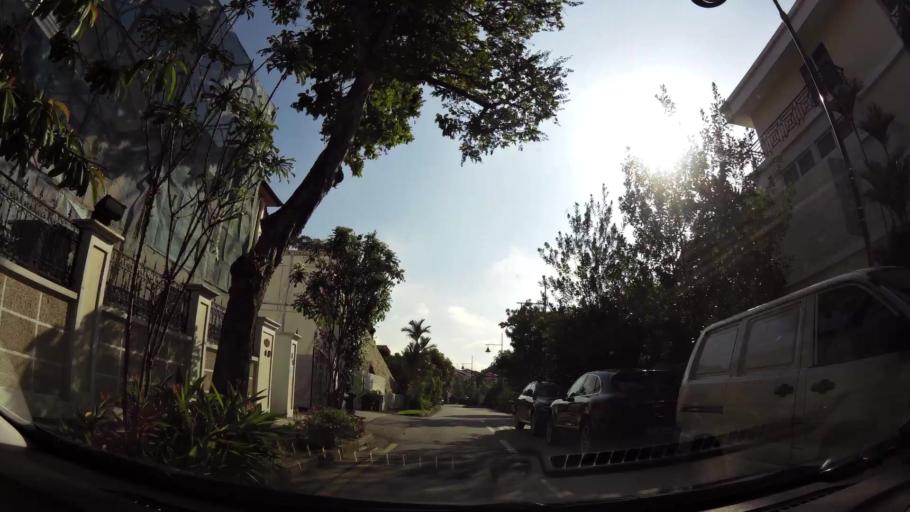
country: SG
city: Singapore
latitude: 1.3168
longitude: 103.9295
